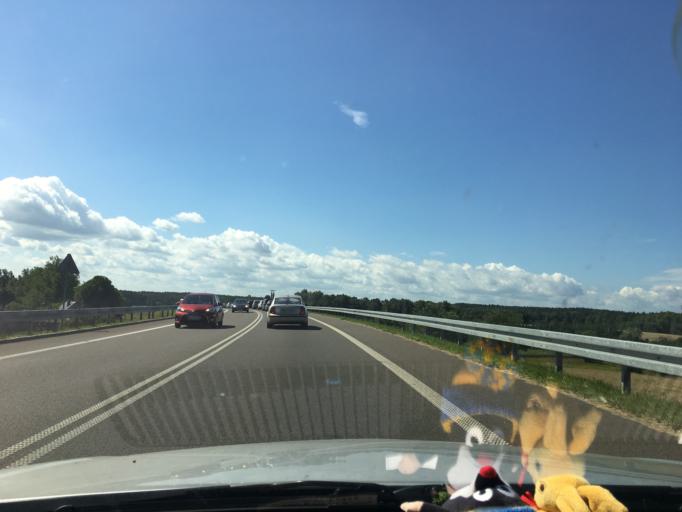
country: PL
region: West Pomeranian Voivodeship
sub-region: Powiat goleniowski
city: Przybiernow
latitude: 53.8470
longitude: 14.7478
